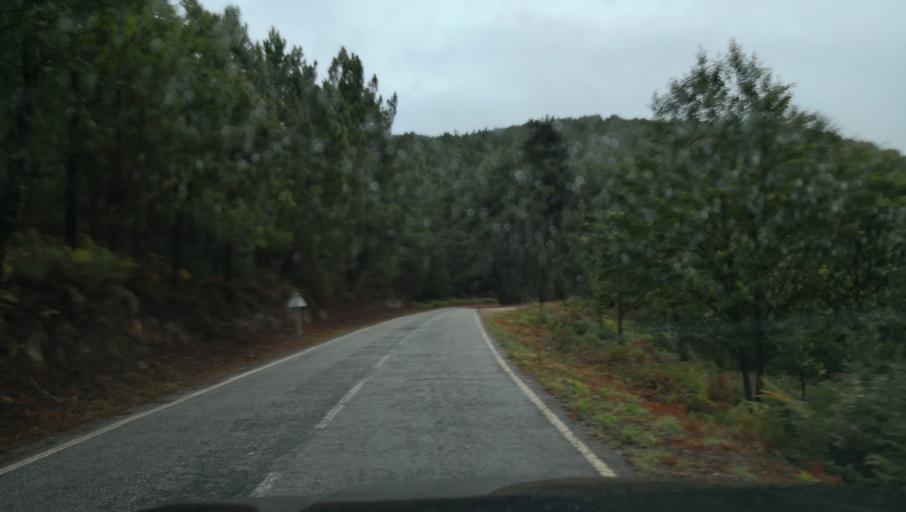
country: PT
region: Vila Real
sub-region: Sabrosa
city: Sabrosa
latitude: 41.3434
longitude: -7.5863
